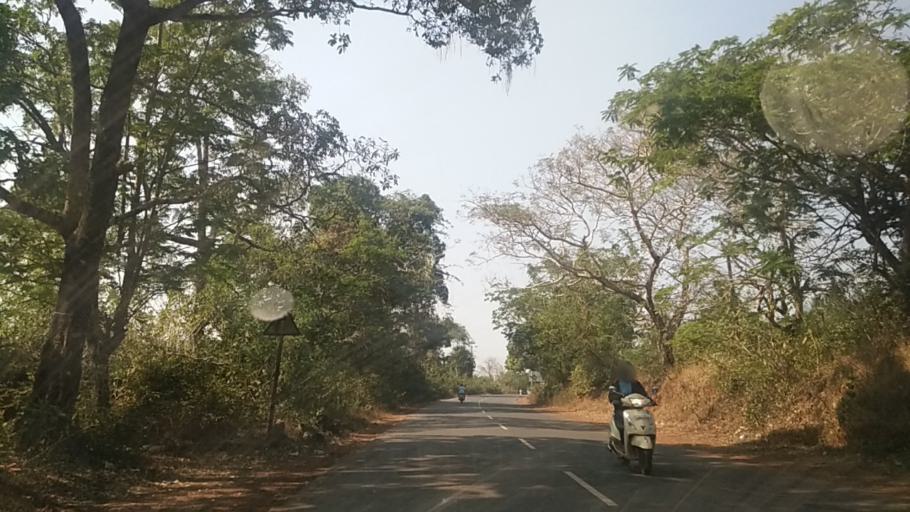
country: IN
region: Goa
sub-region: North Goa
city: Carapur
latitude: 15.5797
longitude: 73.9718
